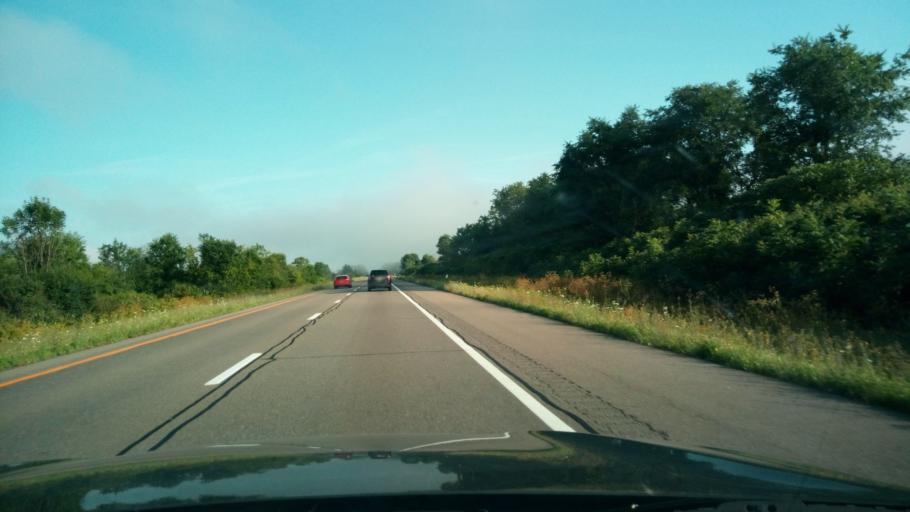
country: US
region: New York
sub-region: Steuben County
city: Gang Mills
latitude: 42.2498
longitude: -77.2029
